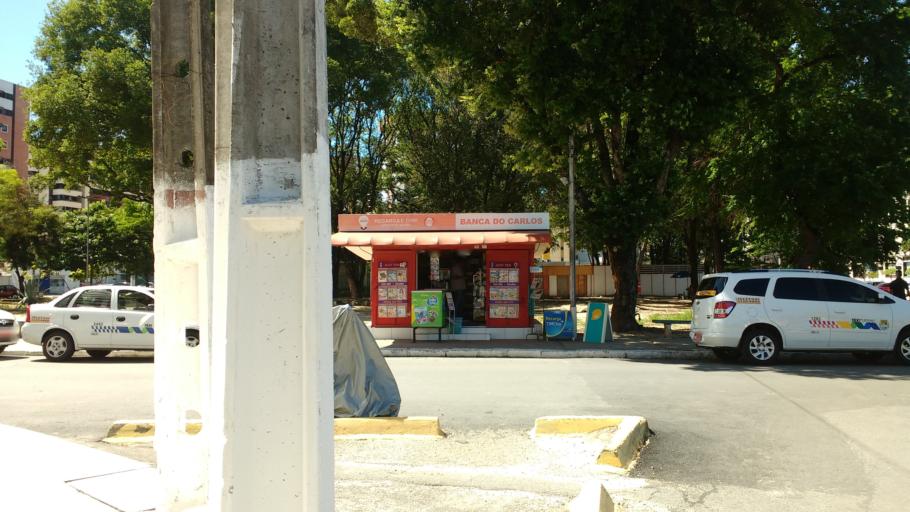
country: BR
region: Alagoas
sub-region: Maceio
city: Maceio
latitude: -9.6631
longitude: -35.7097
